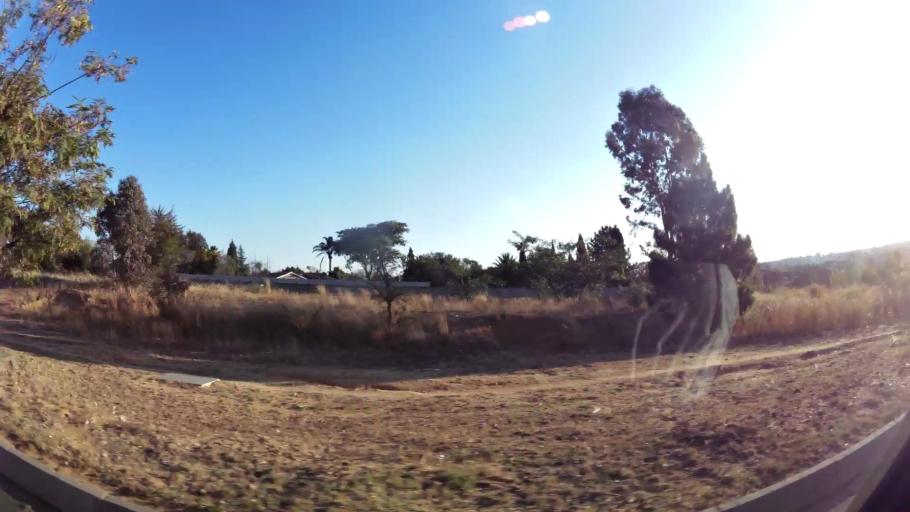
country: ZA
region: Gauteng
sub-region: City of Johannesburg Metropolitan Municipality
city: Midrand
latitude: -25.9991
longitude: 28.1184
